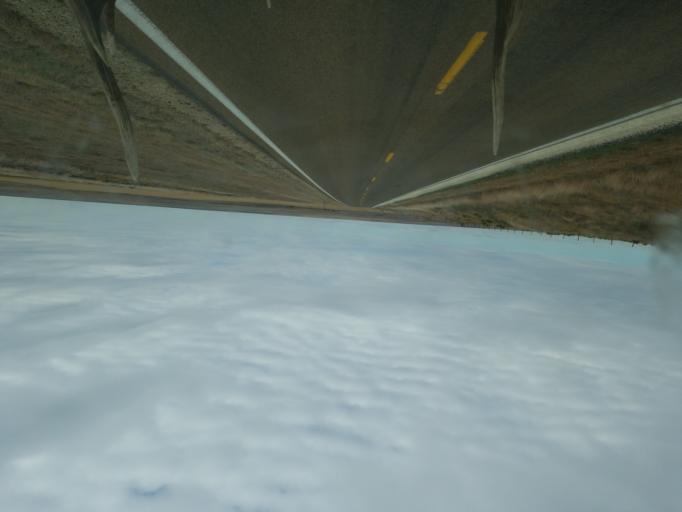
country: US
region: Kansas
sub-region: Wallace County
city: Sharon Springs
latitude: 39.0072
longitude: -101.3737
